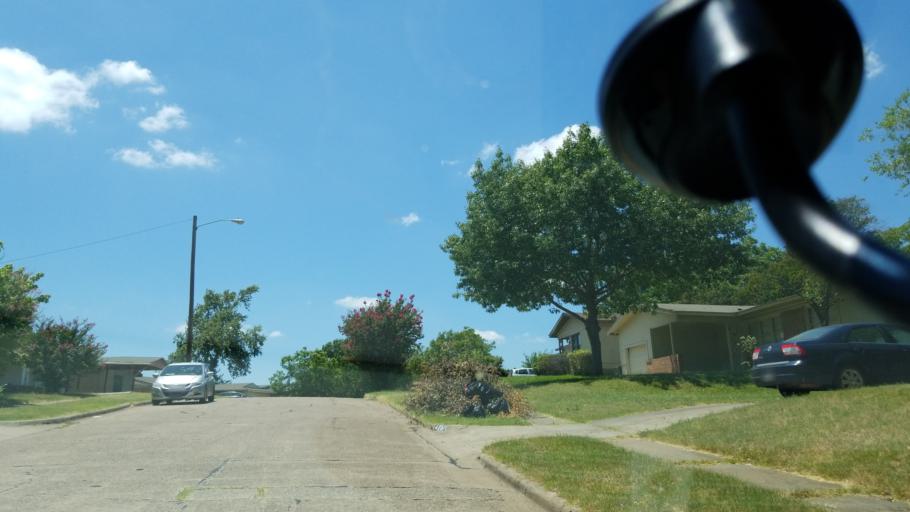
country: US
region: Texas
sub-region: Dallas County
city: Cockrell Hill
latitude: 32.6928
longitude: -96.8151
